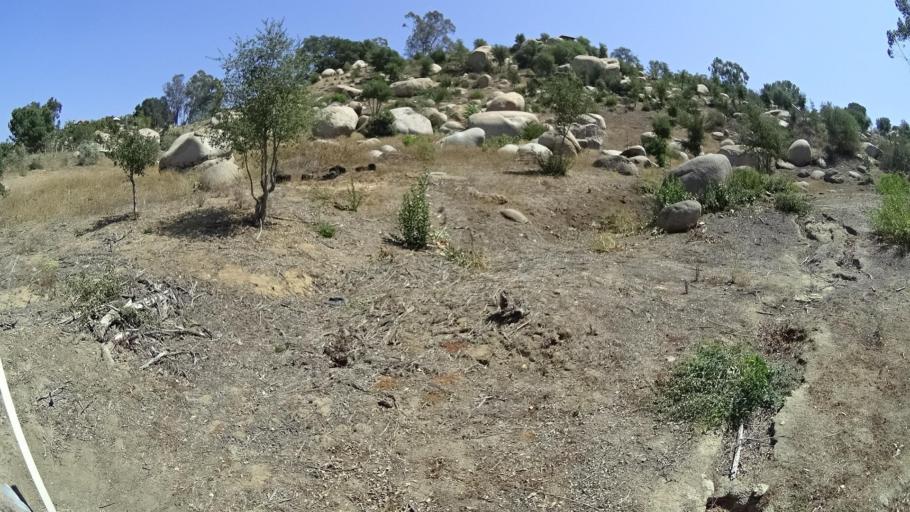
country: US
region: California
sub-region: San Diego County
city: Fallbrook
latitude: 33.4377
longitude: -117.2828
